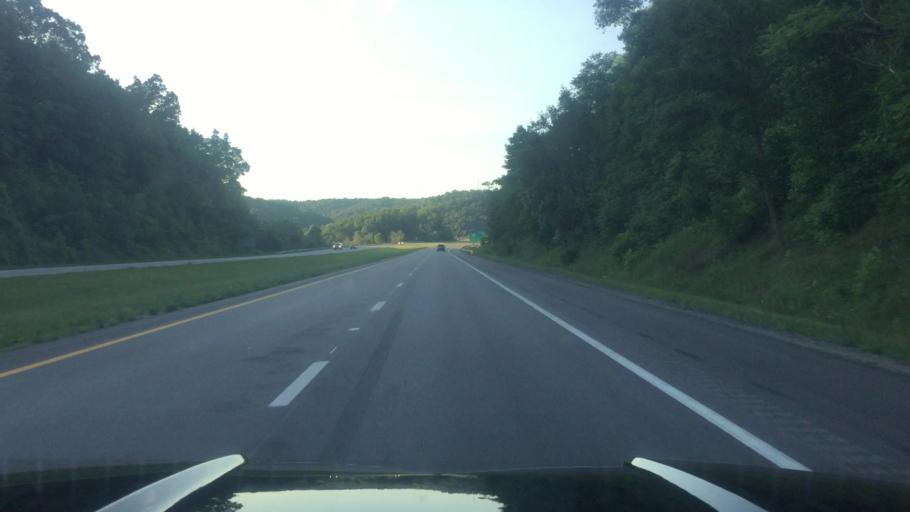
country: US
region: Ohio
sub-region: Guernsey County
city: Cambridge
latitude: 40.1374
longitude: -81.5521
